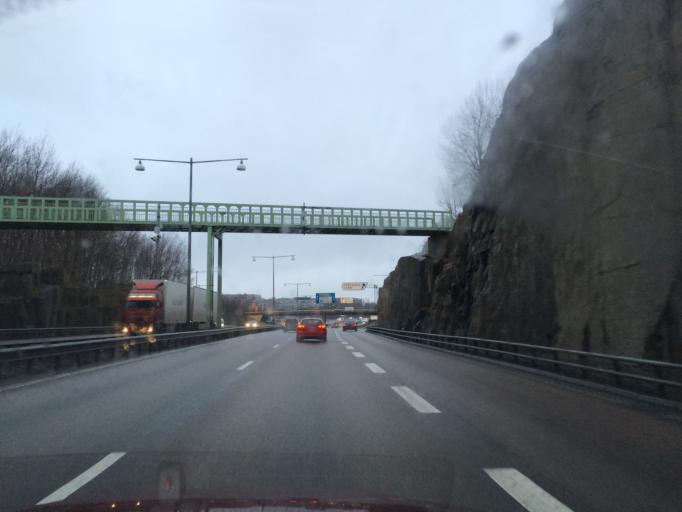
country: SE
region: Vaestra Goetaland
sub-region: Goteborg
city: Majorna
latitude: 57.6470
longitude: 11.9215
